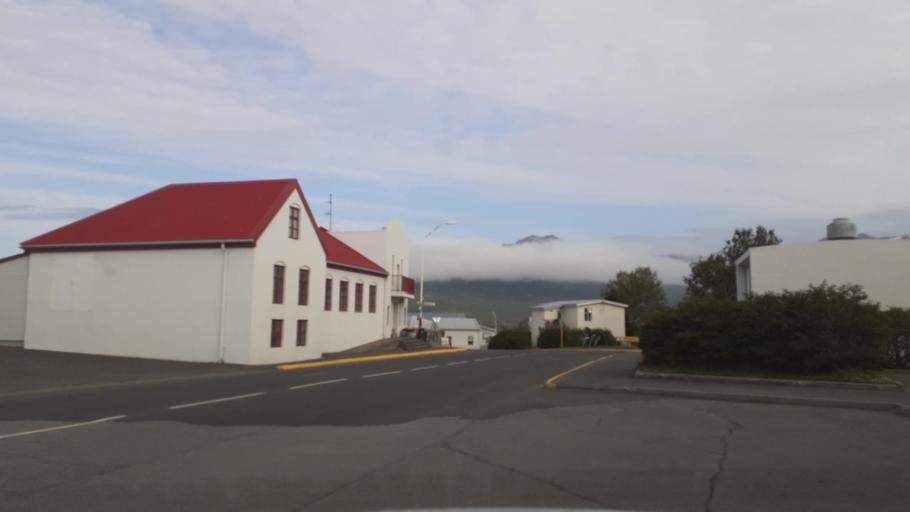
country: IS
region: Northeast
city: Dalvik
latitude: 65.9699
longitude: -18.5278
